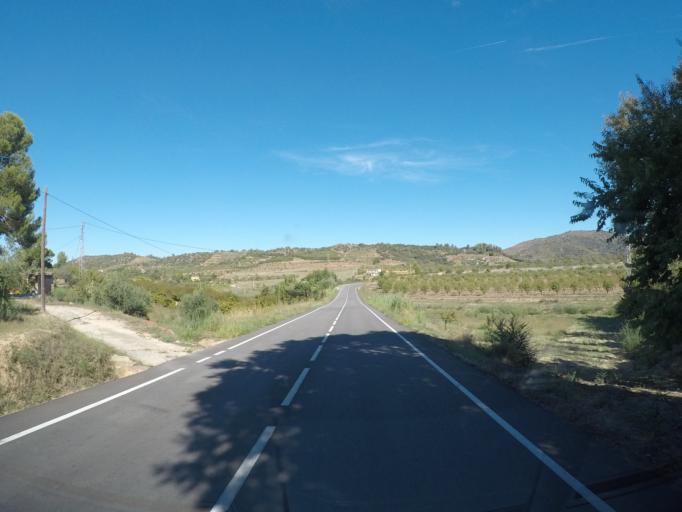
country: ES
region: Catalonia
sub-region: Provincia de Tarragona
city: Falset
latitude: 41.1550
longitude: 0.8160
